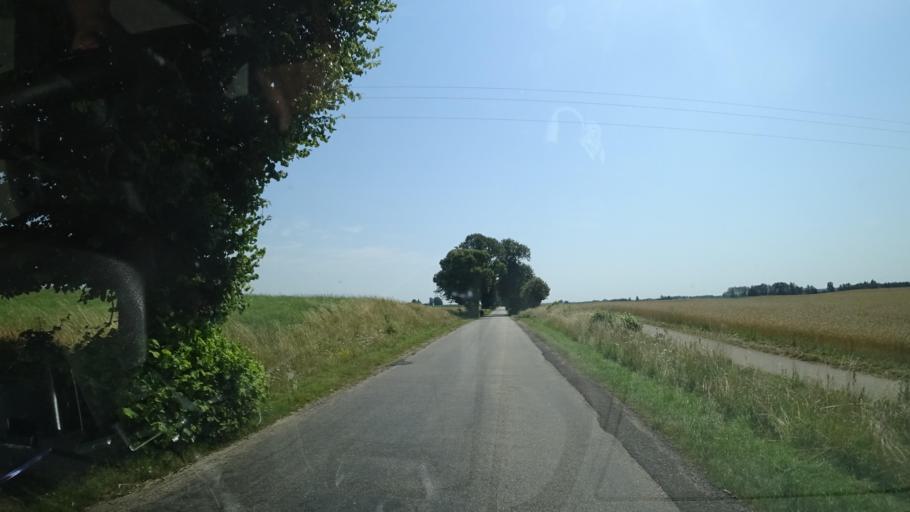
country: PL
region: Pomeranian Voivodeship
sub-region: Powiat chojnicki
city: Brusy
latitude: 53.8799
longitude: 17.6477
